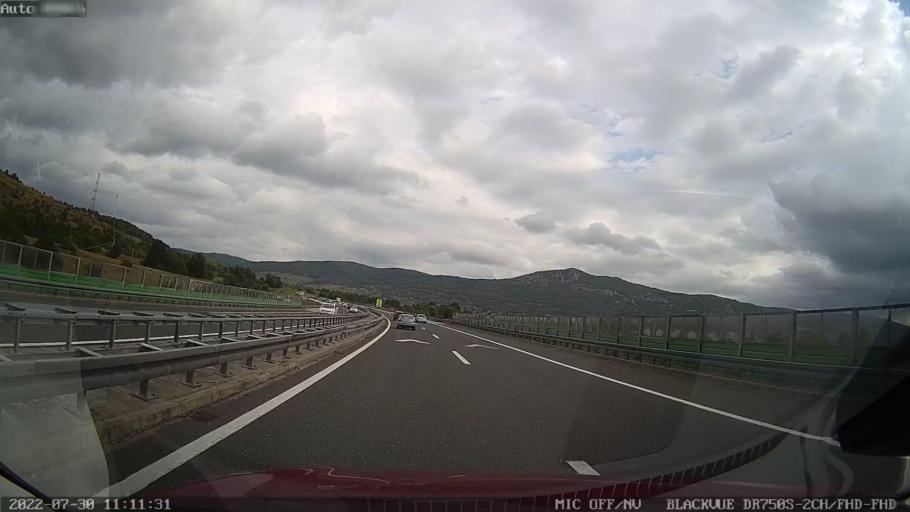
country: HR
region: Licko-Senjska
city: Brinje
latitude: 44.9317
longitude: 15.1723
